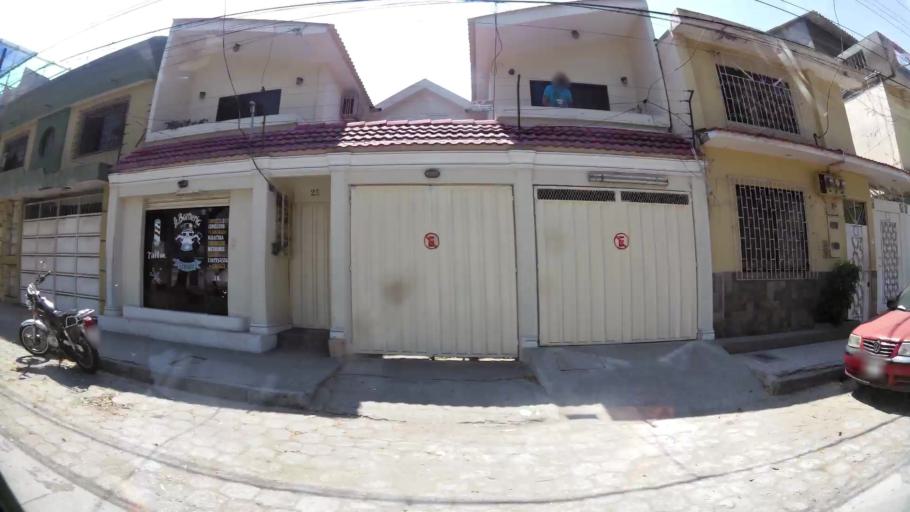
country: EC
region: Guayas
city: Eloy Alfaro
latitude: -2.1207
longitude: -79.9030
